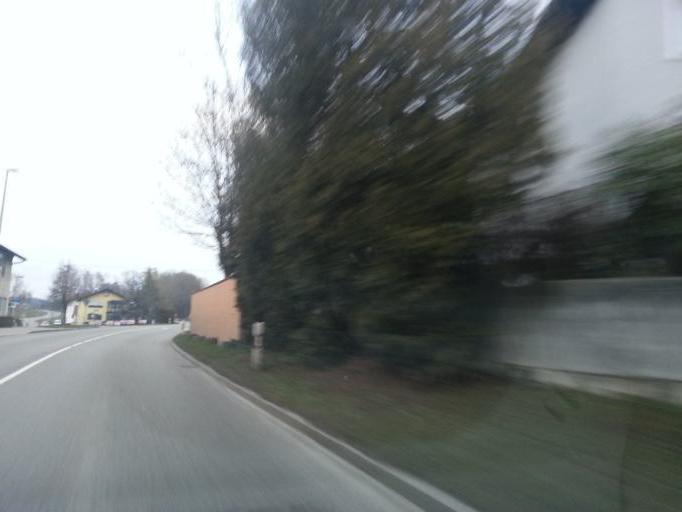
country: DE
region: Baden-Wuerttemberg
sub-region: Tuebingen Region
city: Oberteuringen
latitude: 47.7416
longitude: 9.4837
